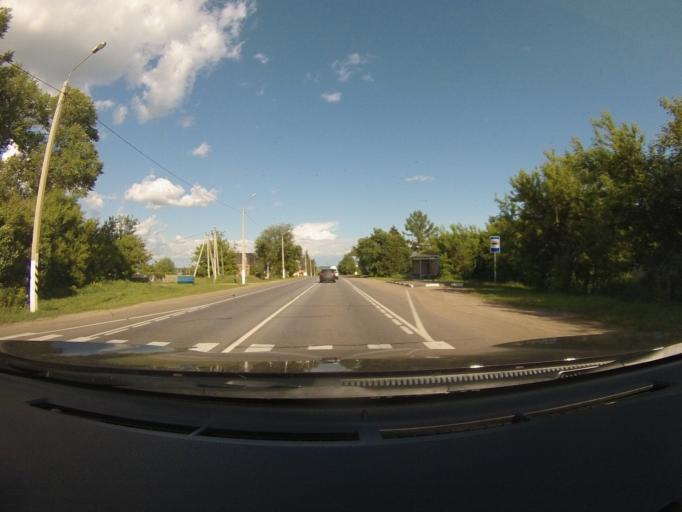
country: RU
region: Tula
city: Bol'shoye Skuratovo
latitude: 53.4537
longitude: 36.8741
